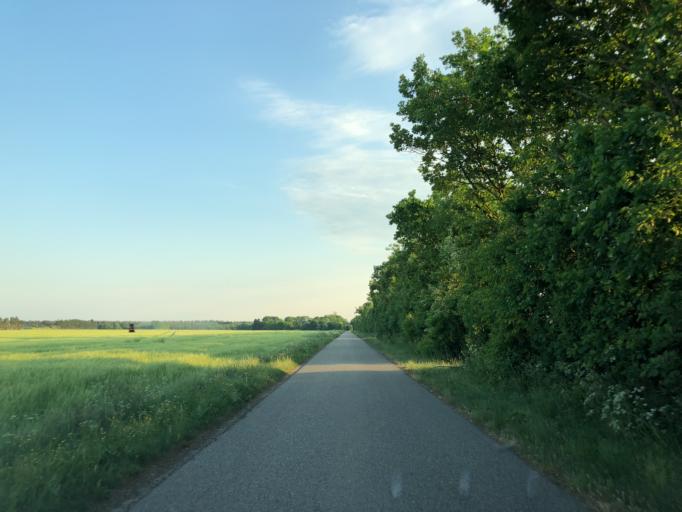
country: DK
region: Central Jutland
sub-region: Holstebro Kommune
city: Holstebro
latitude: 56.3805
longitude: 8.4631
